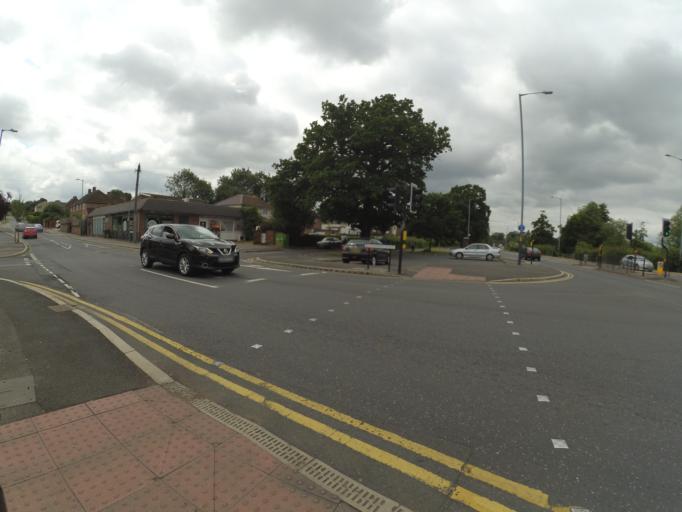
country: GB
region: England
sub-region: Warwickshire
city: Rugby
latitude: 52.3666
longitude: -1.2781
